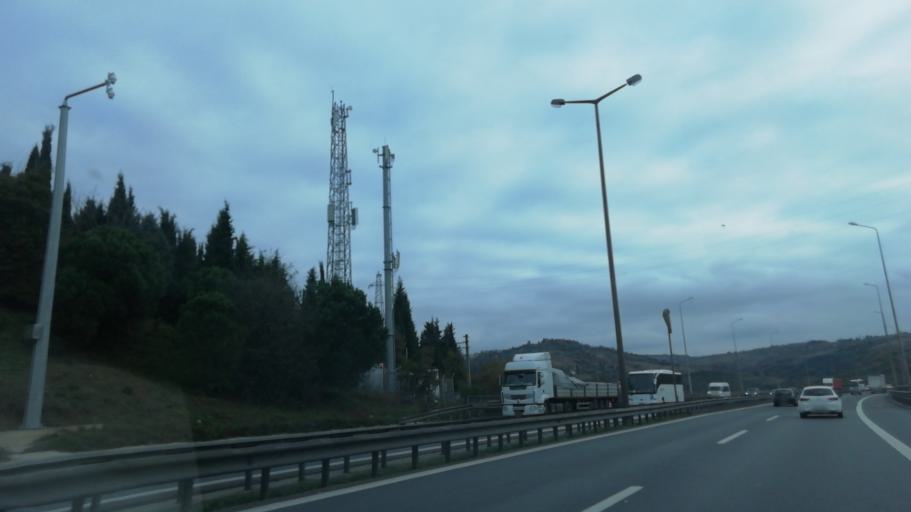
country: TR
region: Kocaeli
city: Izmit
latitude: 40.7779
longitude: 29.8786
